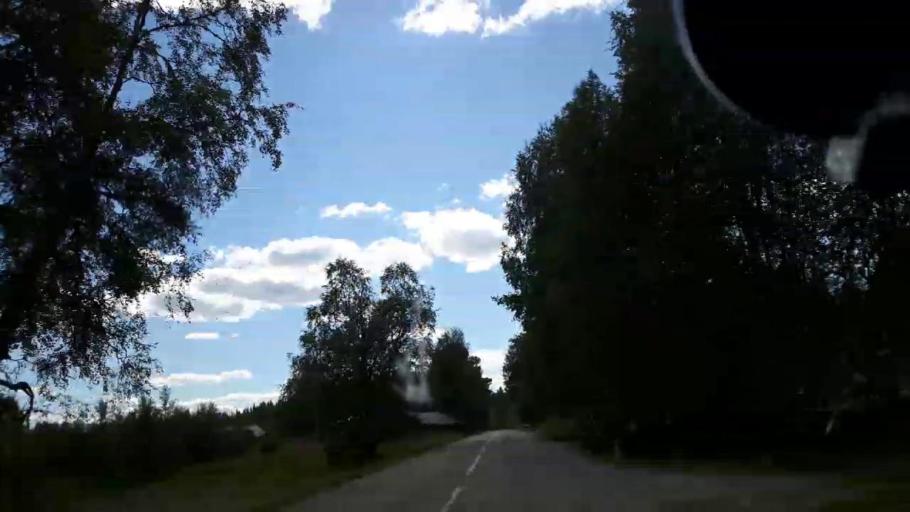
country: SE
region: Jaemtland
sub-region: Ragunda Kommun
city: Hammarstrand
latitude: 62.8974
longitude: 16.2276
